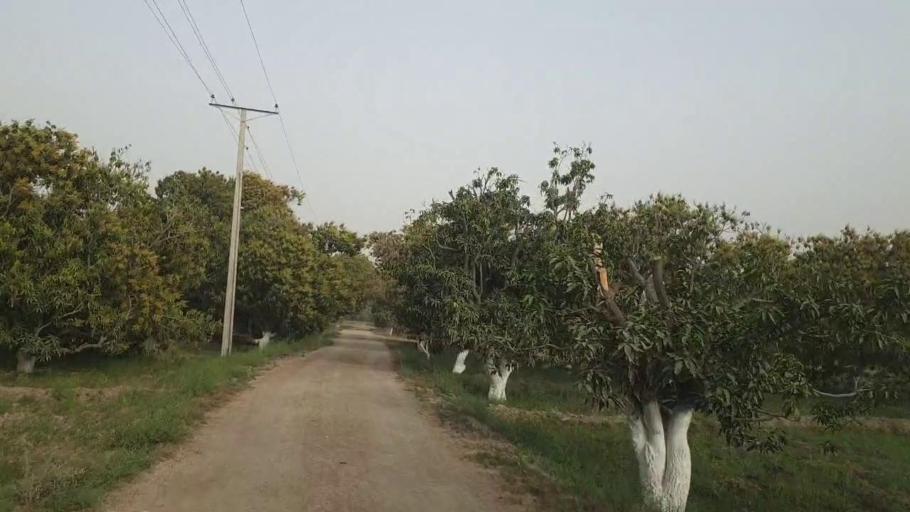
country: PK
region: Sindh
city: Kunri
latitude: 25.0677
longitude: 69.4405
